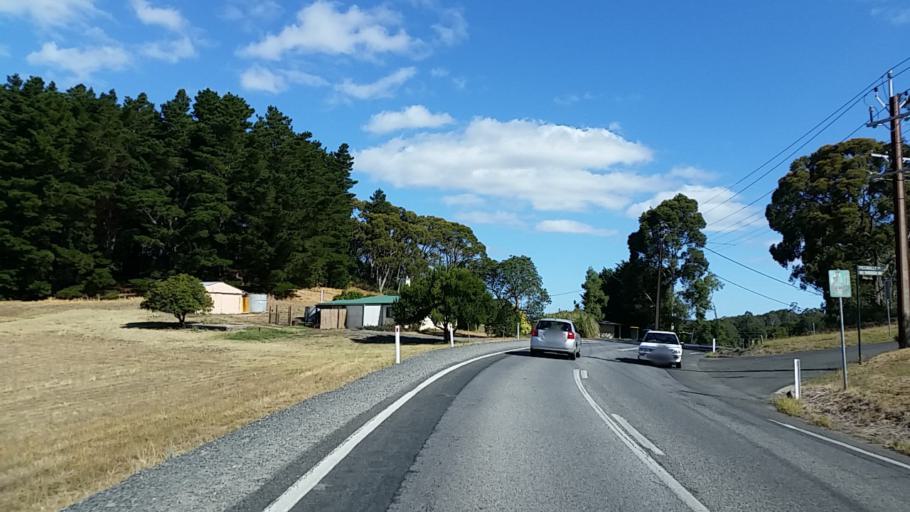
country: AU
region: South Australia
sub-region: Adelaide Hills
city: Bridgewater
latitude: -34.9735
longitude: 138.7305
